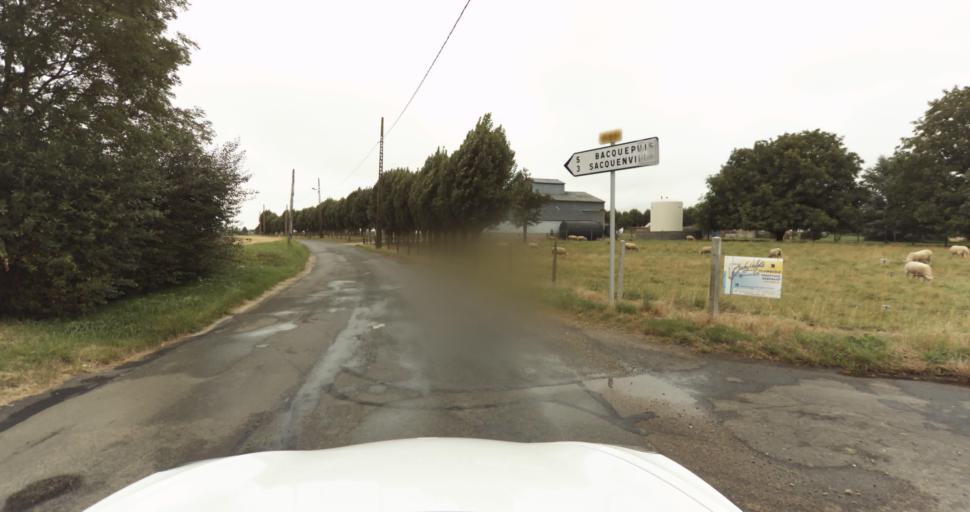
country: FR
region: Haute-Normandie
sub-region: Departement de l'Eure
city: Aviron
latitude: 49.0707
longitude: 1.0968
